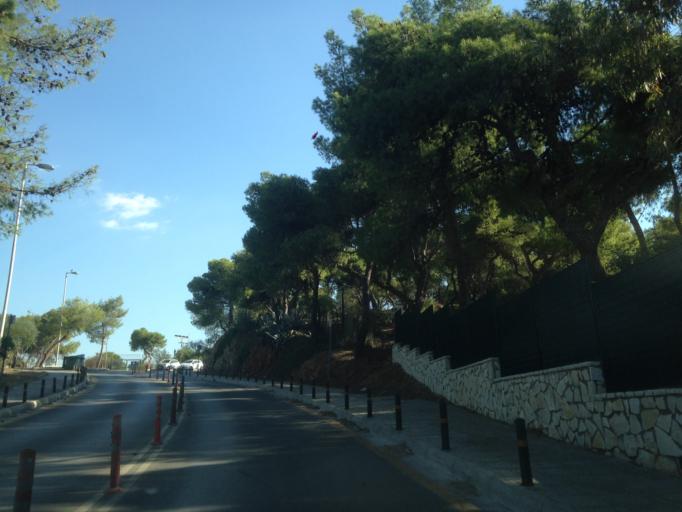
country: GR
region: Attica
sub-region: Nomarchia Anatolikis Attikis
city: Vouliagmeni
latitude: 37.8092
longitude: 23.7745
